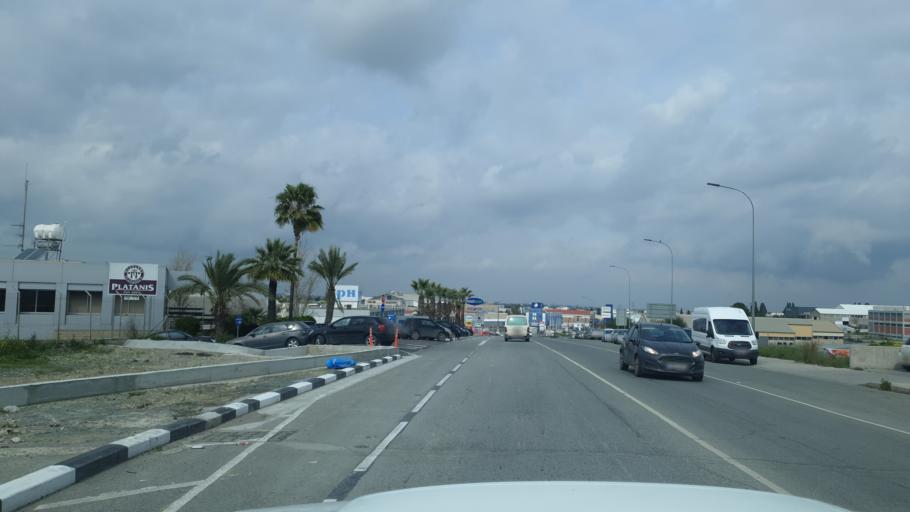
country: CY
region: Lefkosia
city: Geri
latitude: 35.0845
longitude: 33.3806
